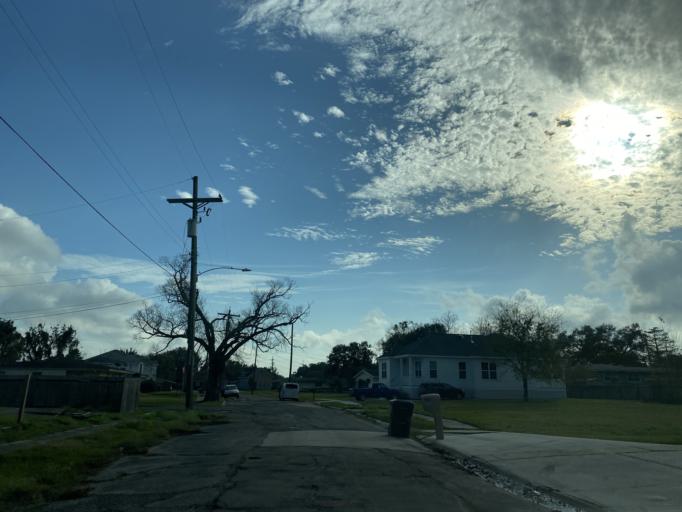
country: US
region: Louisiana
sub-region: Saint Bernard Parish
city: Arabi
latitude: 30.0255
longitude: -90.0378
